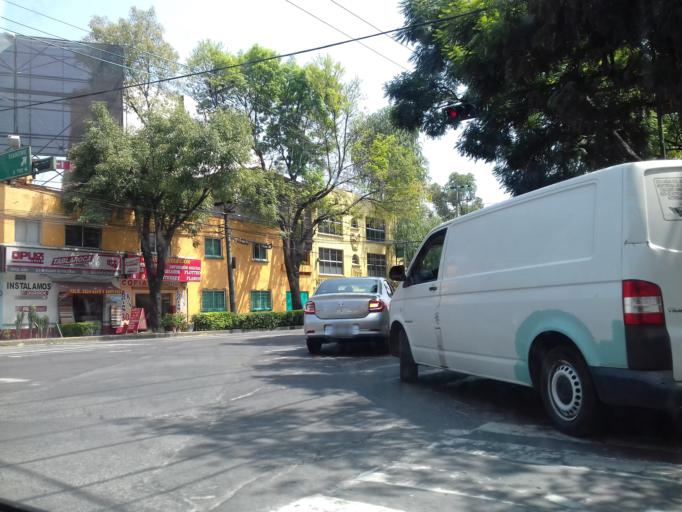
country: MX
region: Mexico City
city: Colonia del Valle
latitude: 19.3665
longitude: -99.1691
